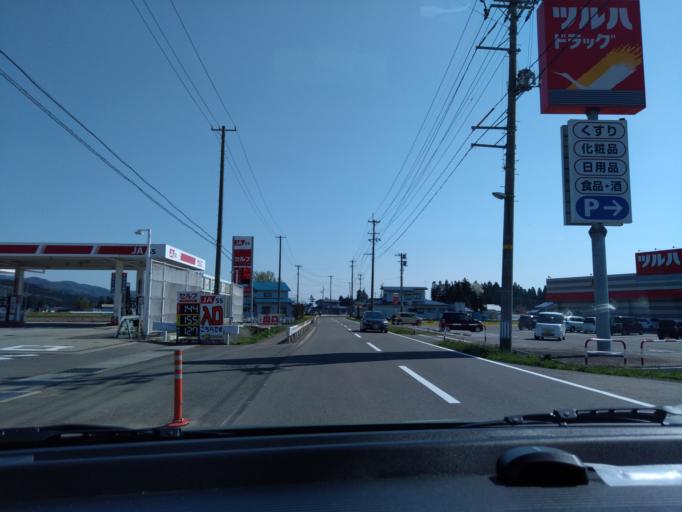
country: JP
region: Akita
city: Omagari
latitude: 39.4598
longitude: 140.5799
